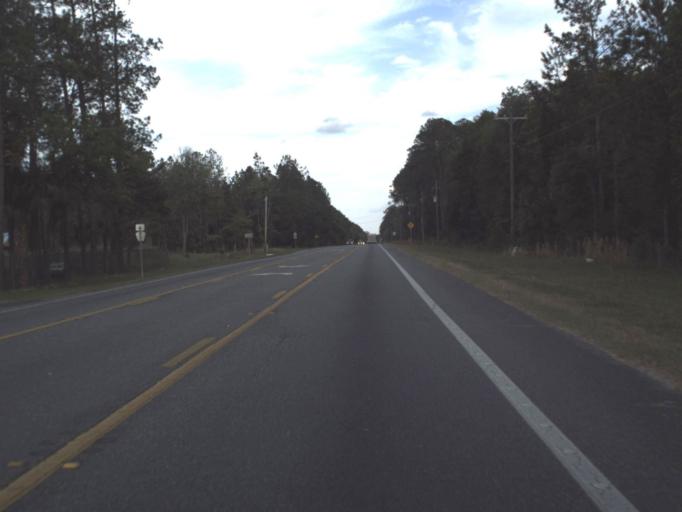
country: US
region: Florida
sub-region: Marion County
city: Silver Springs Shores
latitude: 29.2138
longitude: -81.9731
